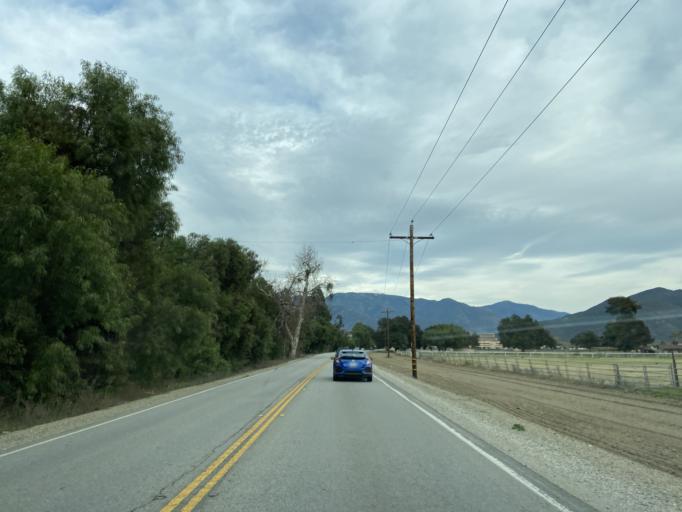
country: US
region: California
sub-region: San Diego County
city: Rainbow
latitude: 33.3645
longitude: -117.0967
